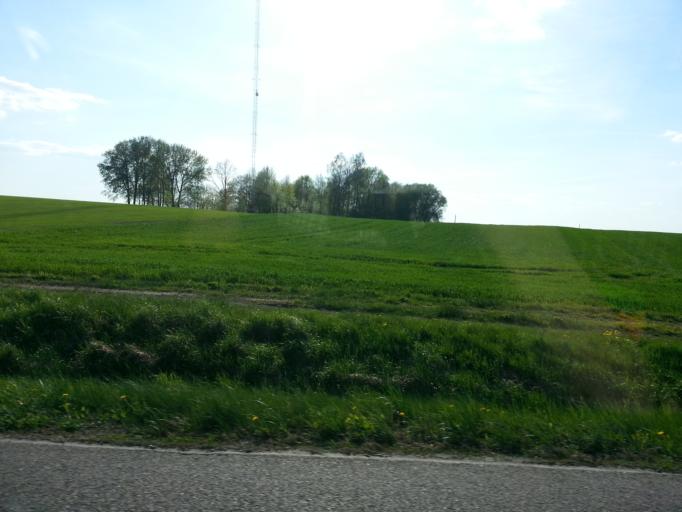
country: LT
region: Panevezys
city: Pasvalys
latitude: 55.9089
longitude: 24.3368
